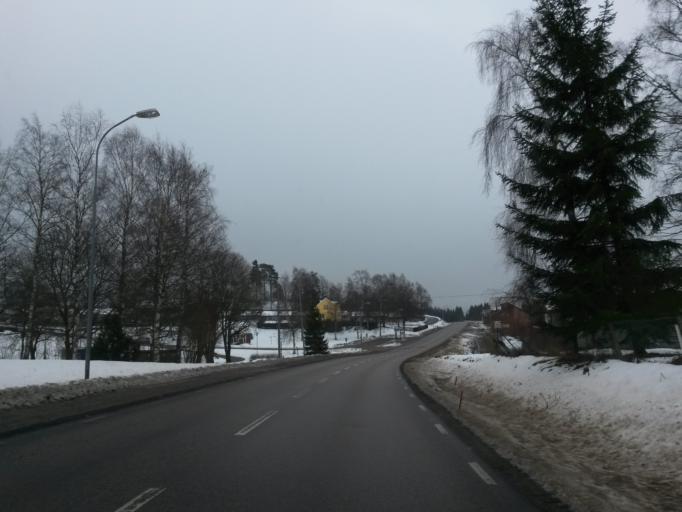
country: SE
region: Vaestra Goetaland
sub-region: Ulricehamns Kommun
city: Ulricehamn
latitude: 57.8993
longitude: 13.3491
